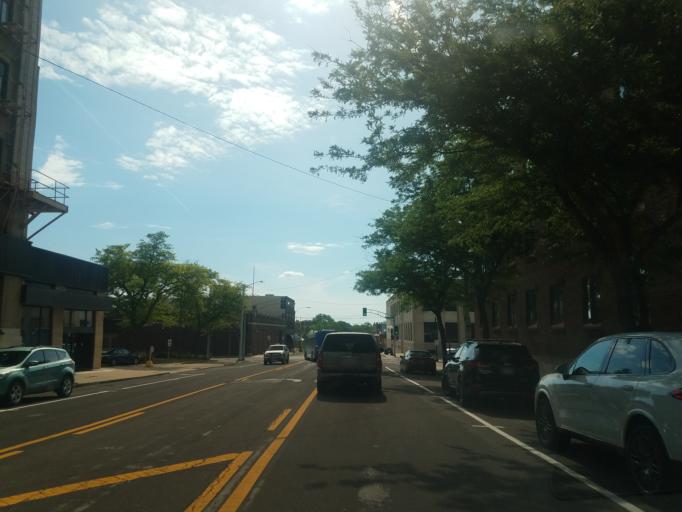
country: US
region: Illinois
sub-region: McLean County
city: Bloomington
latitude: 40.4796
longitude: -88.9948
